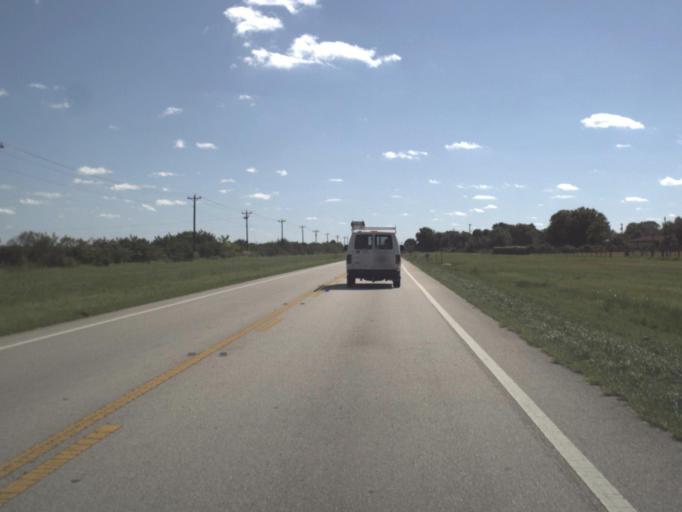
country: US
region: Florida
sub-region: Collier County
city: Immokalee
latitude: 26.4886
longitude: -81.4466
